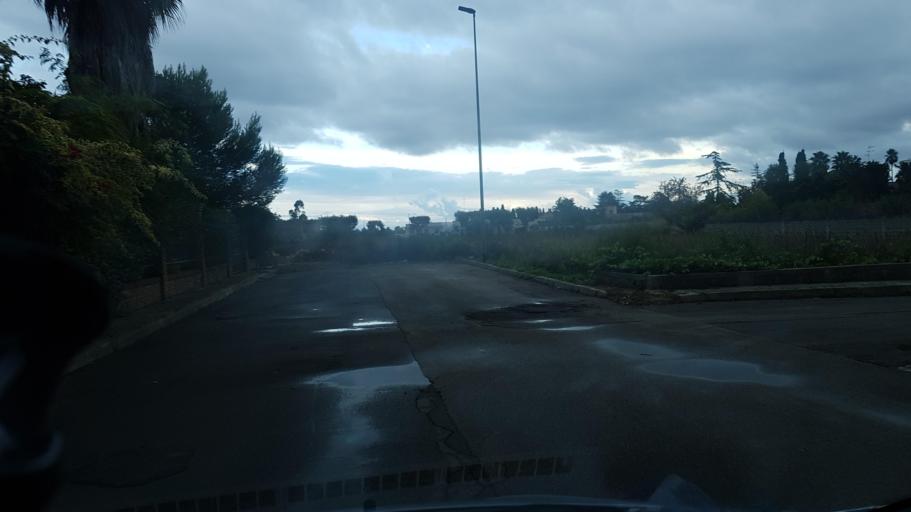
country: IT
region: Apulia
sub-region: Provincia di Lecce
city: Carmiano
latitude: 40.3497
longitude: 18.0509
